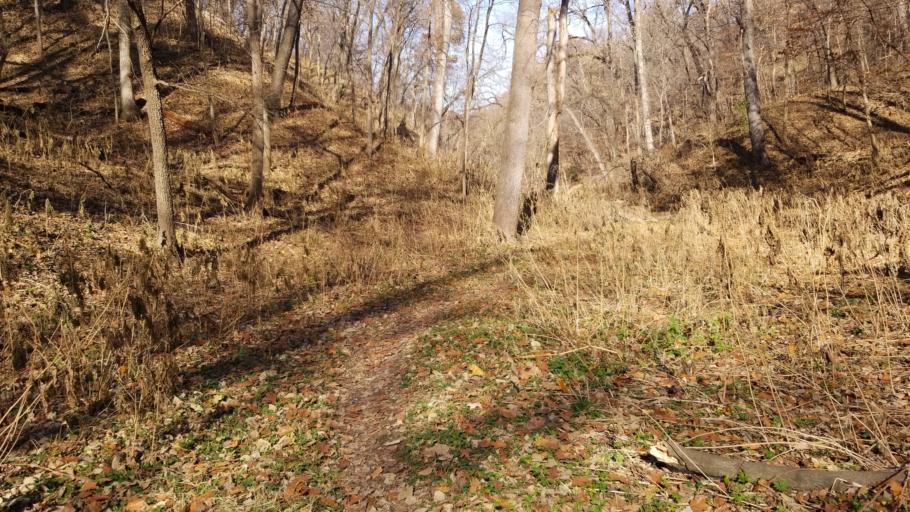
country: US
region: Nebraska
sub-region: Sarpy County
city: Bellevue
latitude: 41.1653
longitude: -95.8941
